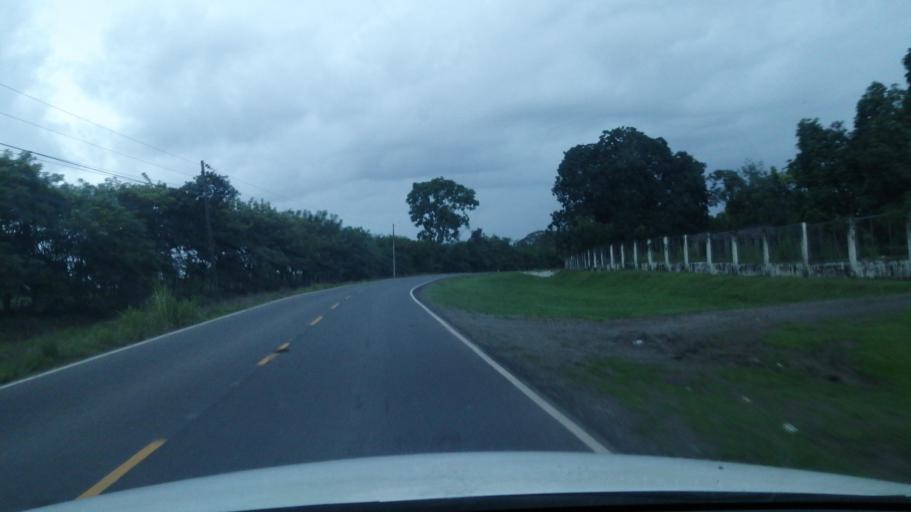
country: PA
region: Chiriqui
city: Pedregal
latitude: 8.3972
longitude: -82.4842
